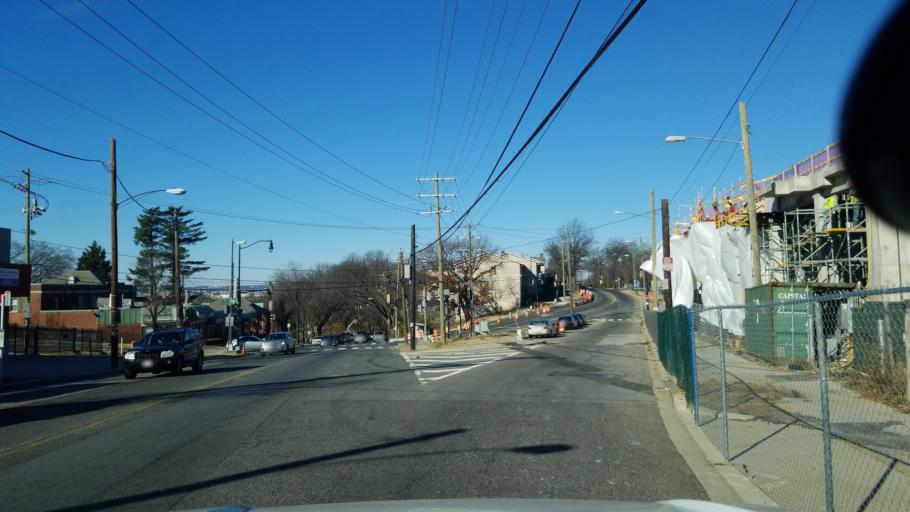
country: US
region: Maryland
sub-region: Prince George's County
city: Hillcrest Heights
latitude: 38.8607
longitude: -76.9688
